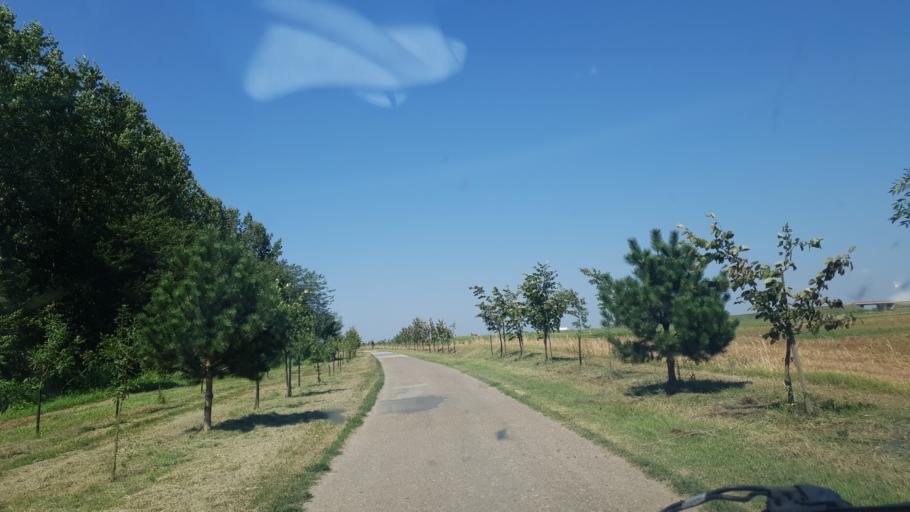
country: RS
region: Autonomna Pokrajina Vojvodina
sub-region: Juznobacki Okrug
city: Kovilj
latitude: 45.2040
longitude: 20.0638
